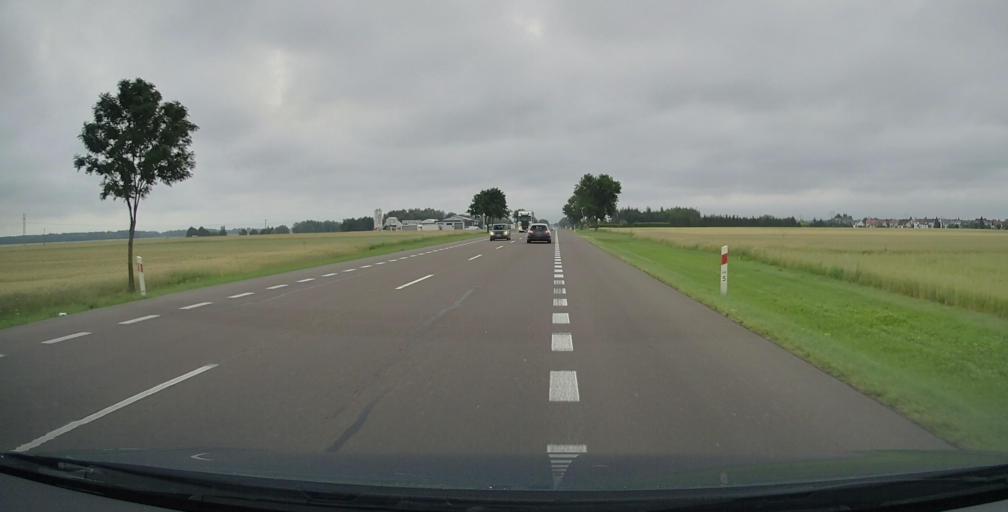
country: PL
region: Lublin Voivodeship
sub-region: Powiat bialski
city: Miedzyrzec Podlaski
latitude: 52.0000
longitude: 22.7919
